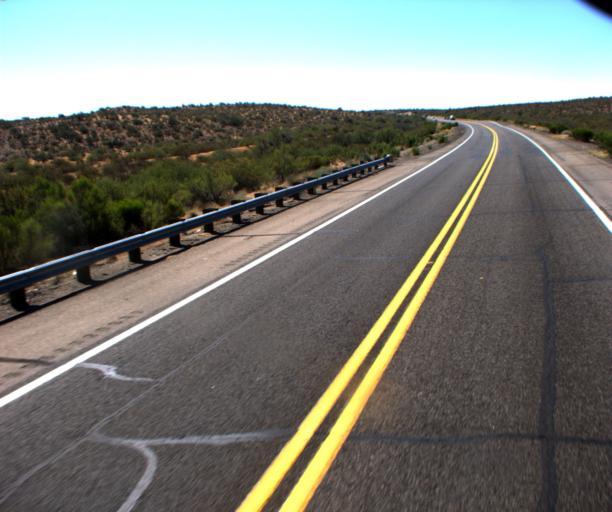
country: US
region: Arizona
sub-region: Yavapai County
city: Congress
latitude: 34.2049
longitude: -113.0638
